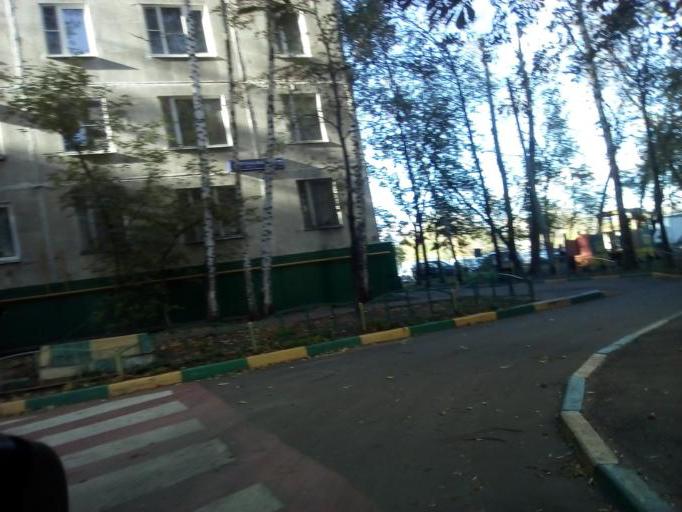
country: RU
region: Moscow
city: Likhobory
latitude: 55.8464
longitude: 37.5555
